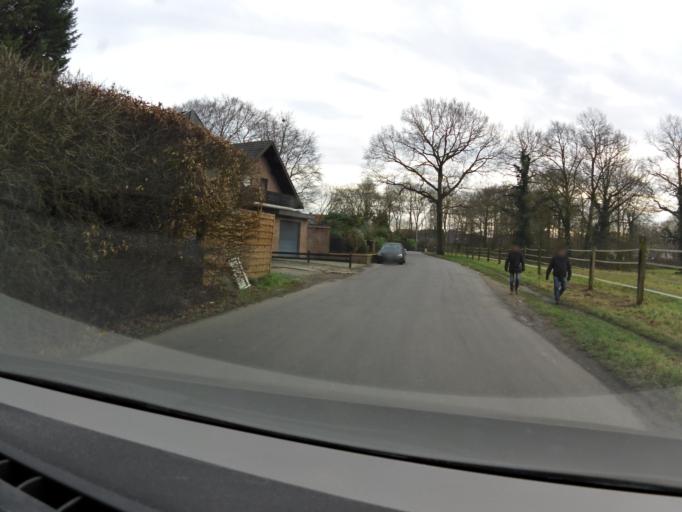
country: DE
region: North Rhine-Westphalia
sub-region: Regierungsbezirk Dusseldorf
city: Nettetal
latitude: 51.3125
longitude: 6.2579
